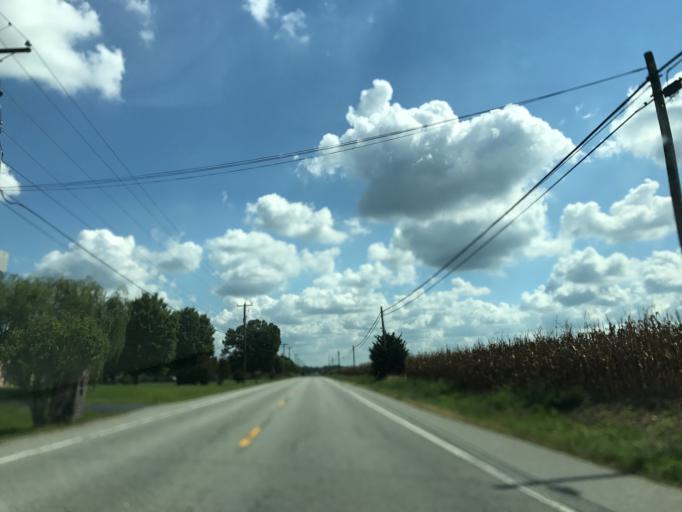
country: US
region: Maryland
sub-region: Queen Anne's County
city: Centreville
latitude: 39.0314
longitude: -76.0445
